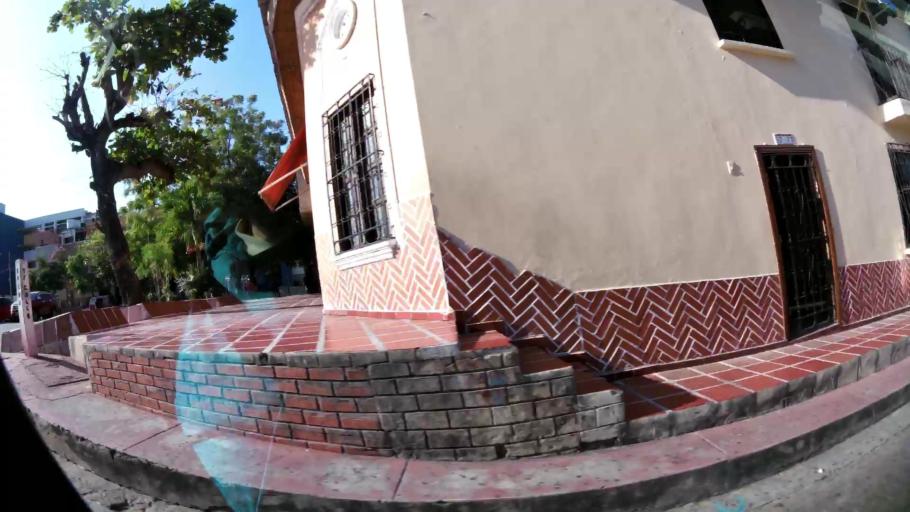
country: CO
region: Atlantico
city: Barranquilla
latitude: 10.9914
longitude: -74.7932
